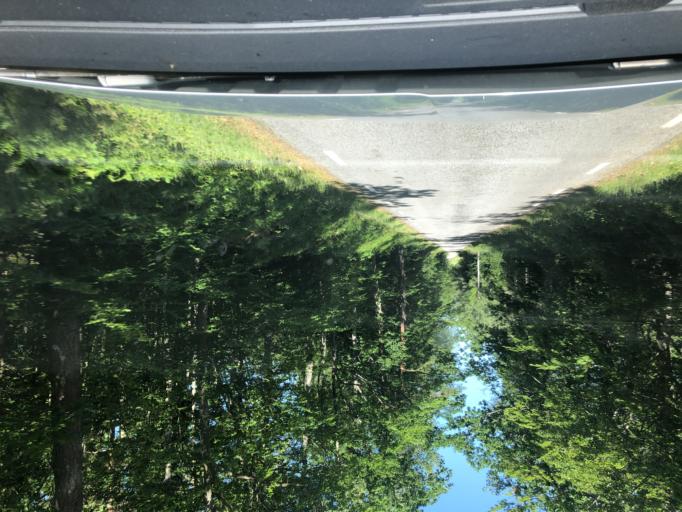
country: SE
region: Blekinge
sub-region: Solvesborgs Kommun
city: Soelvesborg
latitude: 56.1368
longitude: 14.6218
